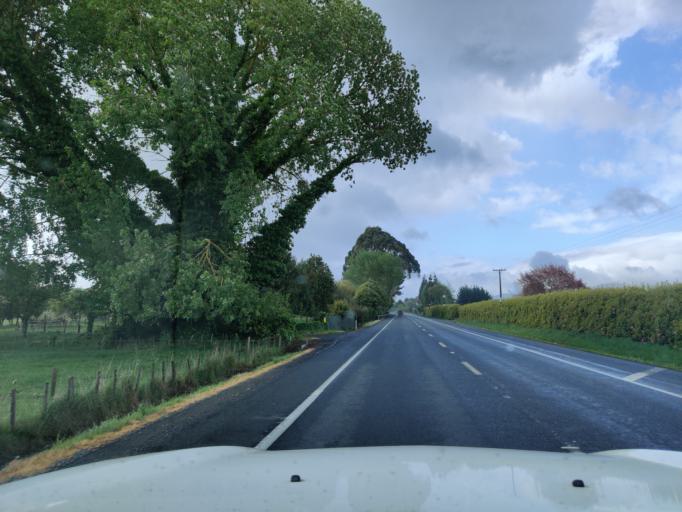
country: NZ
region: Waikato
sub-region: Waipa District
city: Cambridge
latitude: -37.9343
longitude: 175.5739
